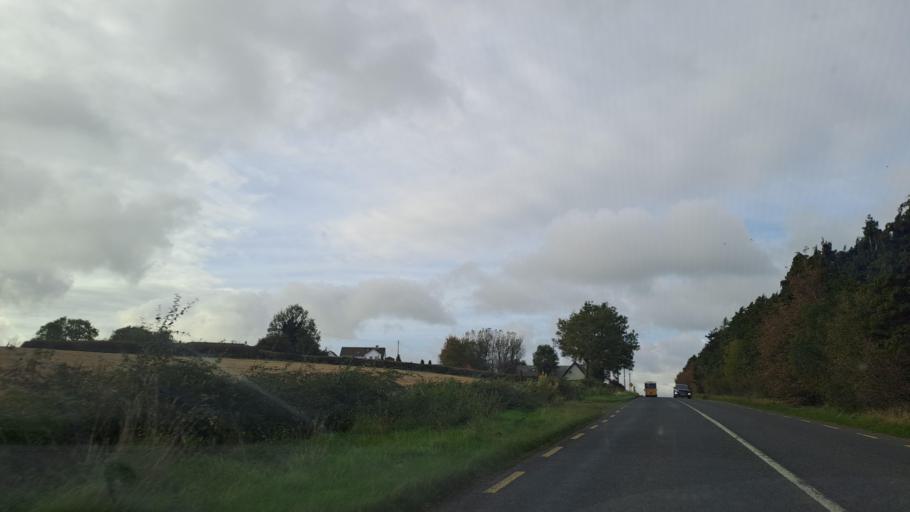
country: IE
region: Ulster
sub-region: An Cabhan
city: Kingscourt
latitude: 53.7894
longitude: -6.7355
